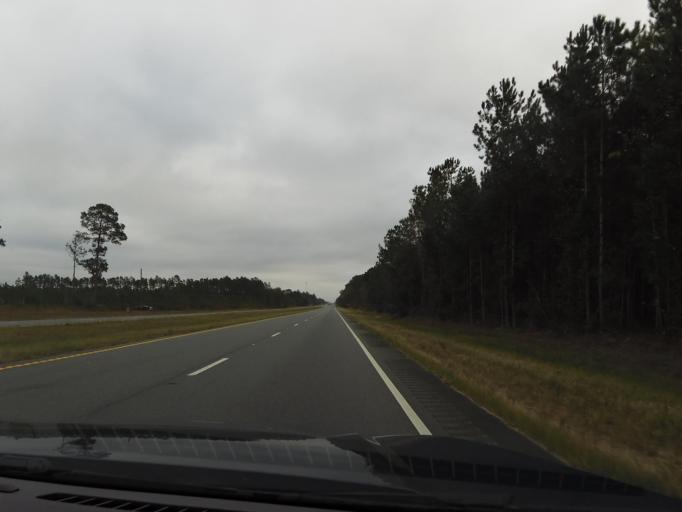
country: US
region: Georgia
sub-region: Charlton County
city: Folkston
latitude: 30.9156
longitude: -82.0825
